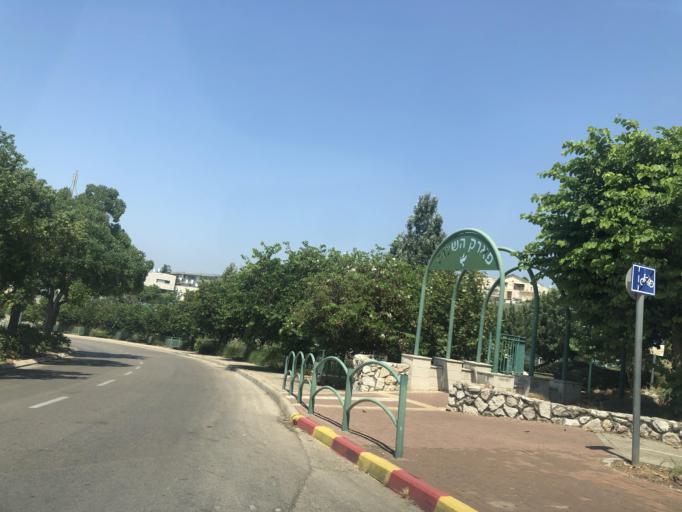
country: IL
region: Haifa
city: Daliyat el Karmil
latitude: 32.6444
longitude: 35.0935
